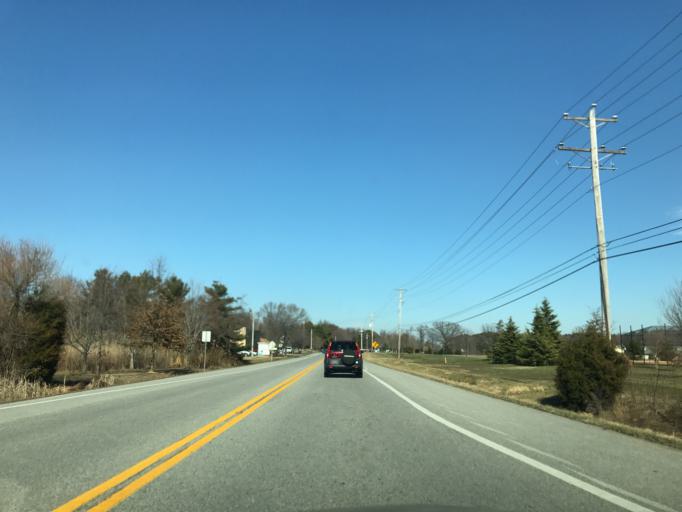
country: US
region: Maryland
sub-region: Queen Anne's County
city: Stevensville
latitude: 38.9601
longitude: -76.3387
